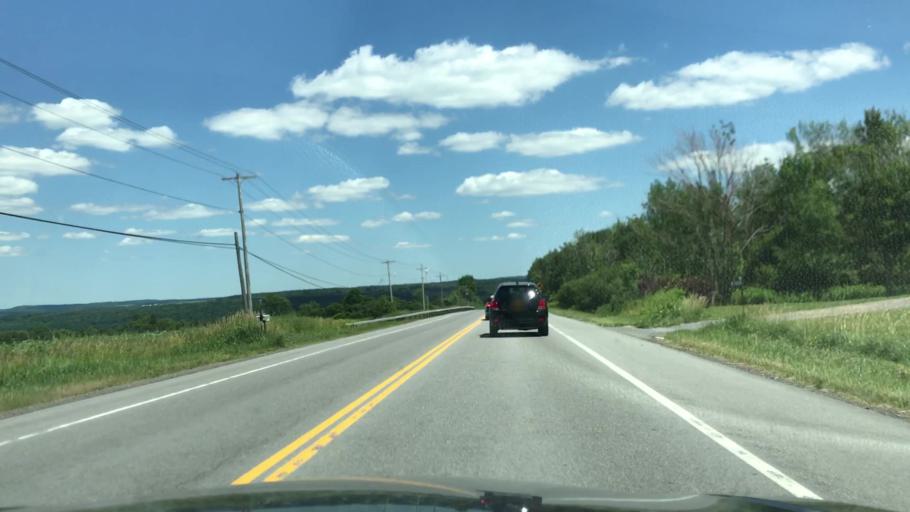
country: US
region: New York
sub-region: Wyoming County
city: Attica
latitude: 42.7705
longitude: -78.3436
